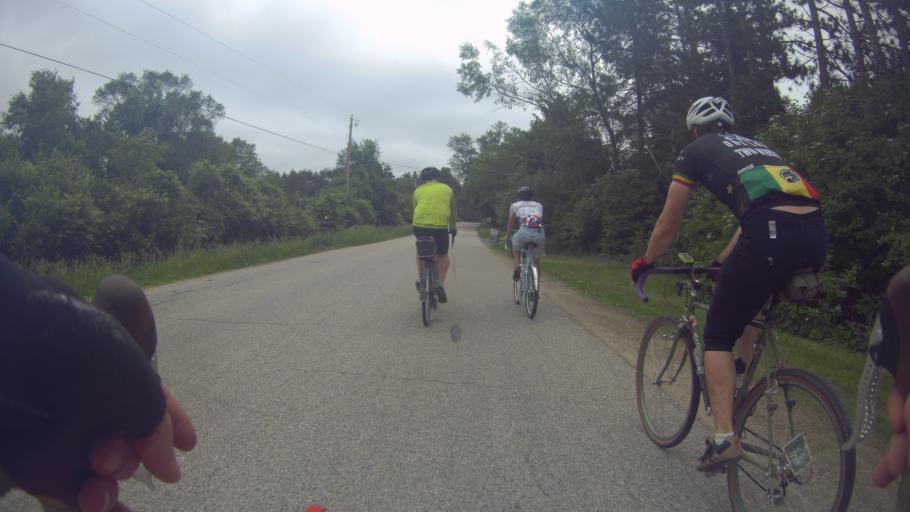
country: US
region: Wisconsin
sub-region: Green County
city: Brooklyn
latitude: 42.8816
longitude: -89.3684
